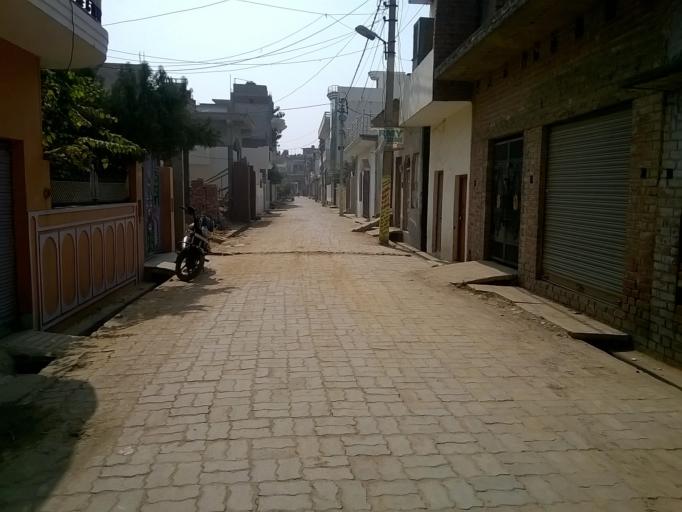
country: IN
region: Uttar Pradesh
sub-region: Etawah
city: Etawah
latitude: 26.7900
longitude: 79.0397
